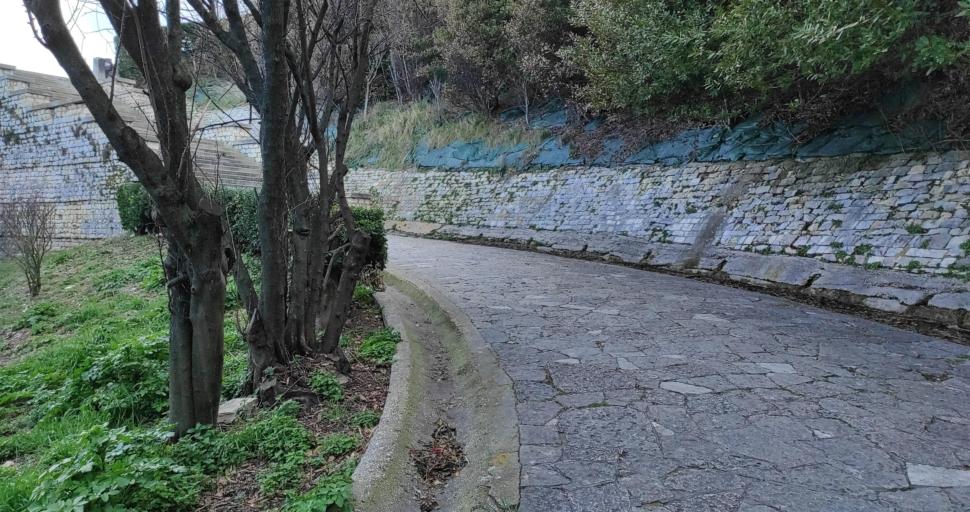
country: IT
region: The Marches
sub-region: Provincia di Ancona
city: Pietra la Croce
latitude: 43.6156
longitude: 13.5338
